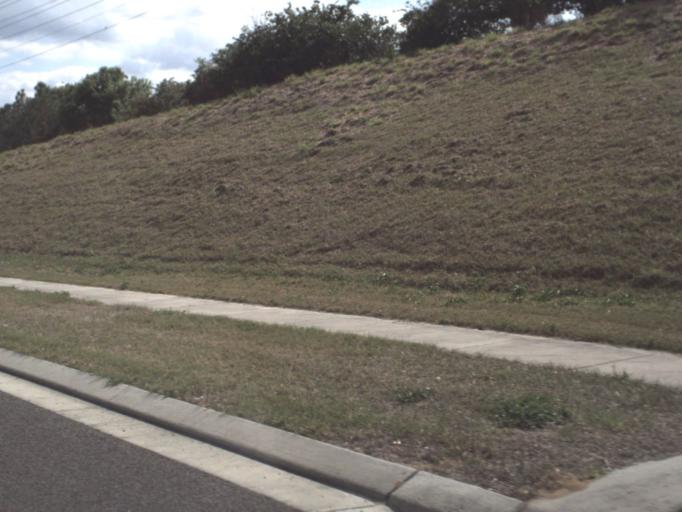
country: US
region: Florida
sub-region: Lake County
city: Clermont
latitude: 28.5093
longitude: -81.7230
